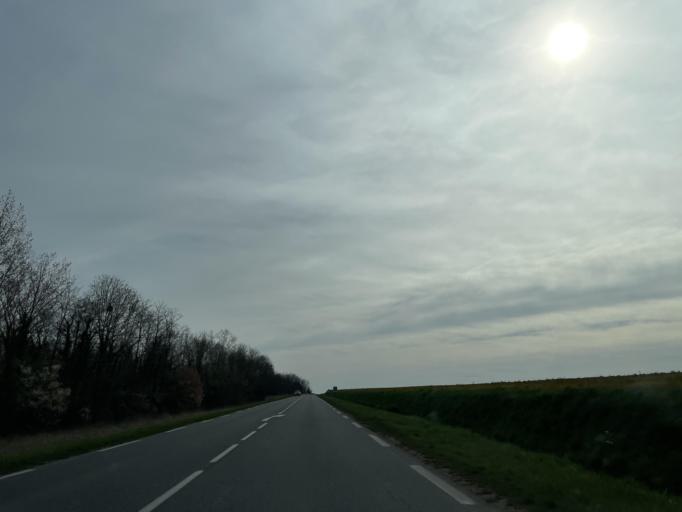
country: FR
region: Ile-de-France
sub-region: Departement de Seine-et-Marne
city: Sourdun
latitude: 48.5493
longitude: 3.3285
